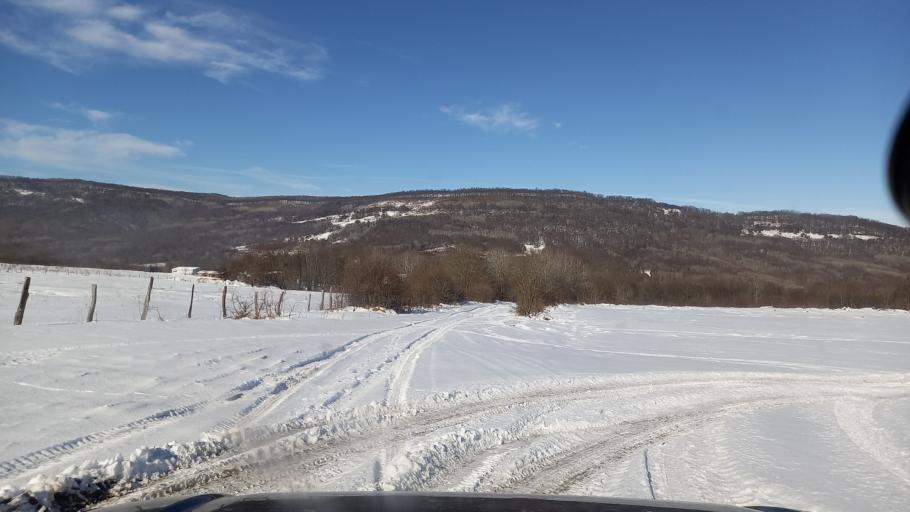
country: RU
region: Adygeya
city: Kamennomostskiy
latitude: 44.2355
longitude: 40.1512
